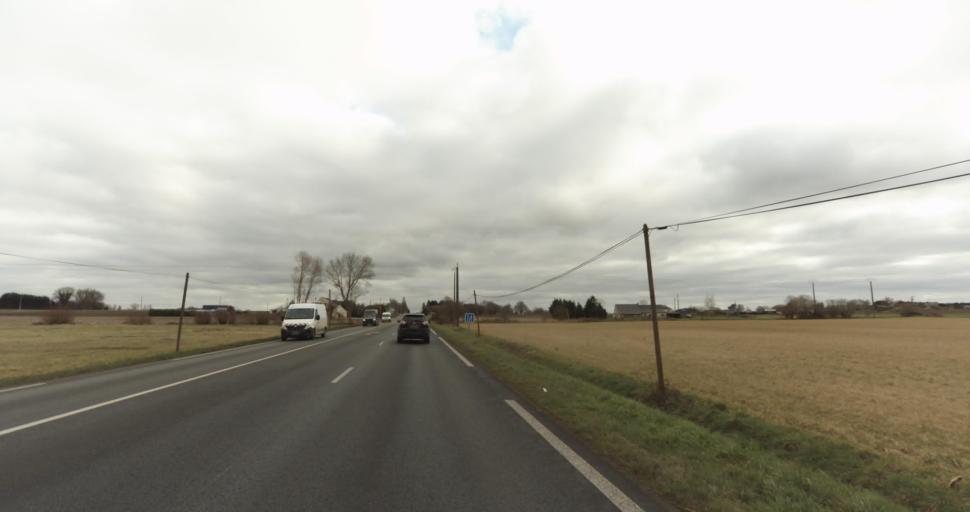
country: FR
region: Pays de la Loire
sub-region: Departement de Maine-et-Loire
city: Vivy
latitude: 47.3639
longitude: -0.0923
